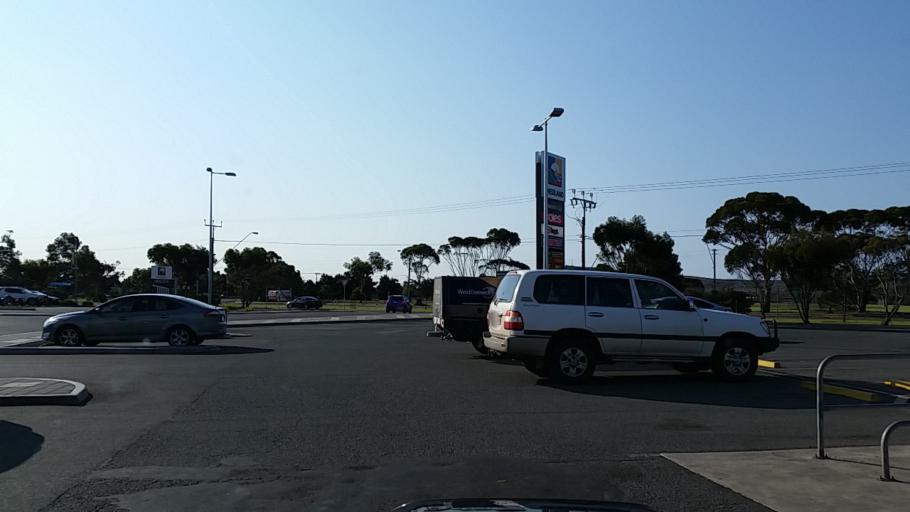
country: AU
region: South Australia
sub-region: Whyalla
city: Whyalla
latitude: -33.0269
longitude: 137.5327
